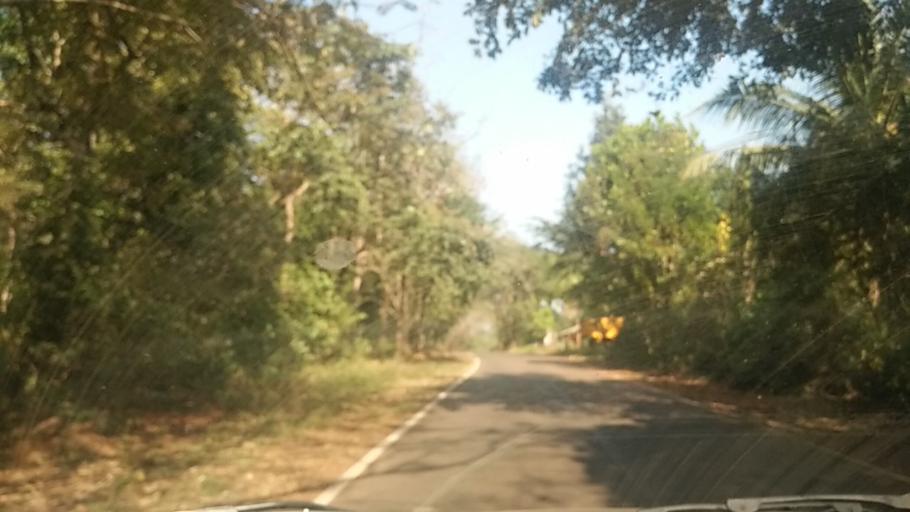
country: IN
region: Goa
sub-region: South Goa
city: Sanguem
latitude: 15.2139
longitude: 74.2047
